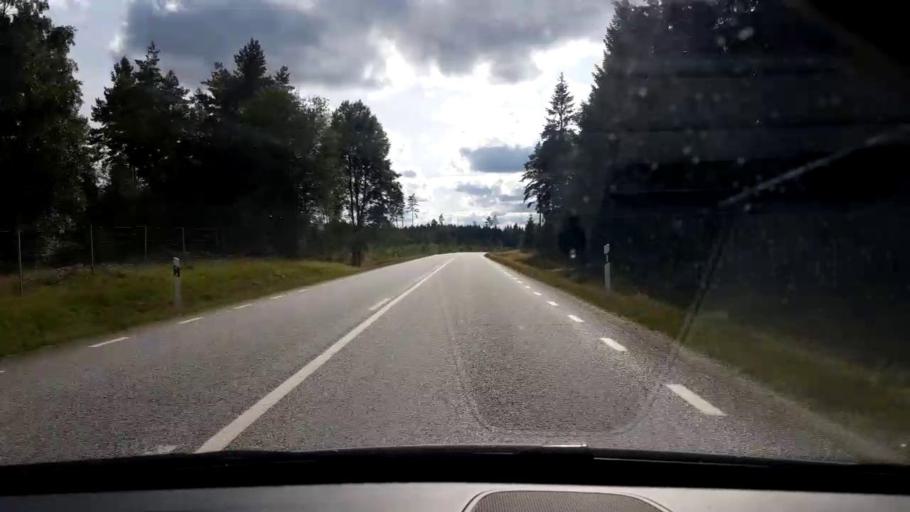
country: SE
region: Joenkoeping
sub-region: Savsjo Kommun
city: Vrigstad
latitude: 57.3704
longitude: 14.5191
